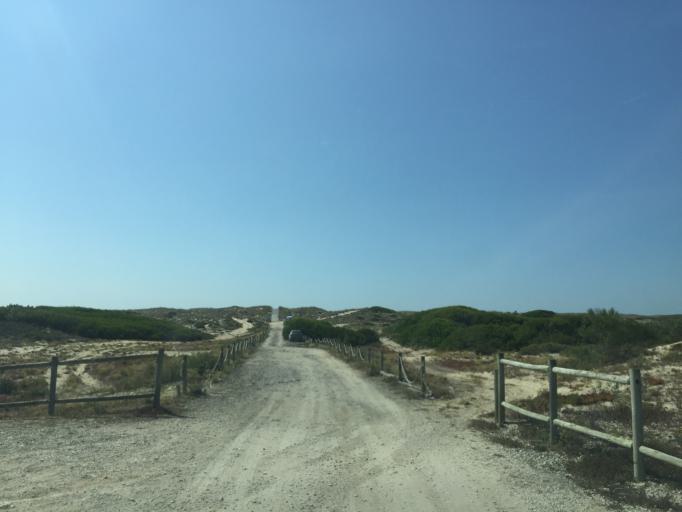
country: PT
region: Coimbra
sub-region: Figueira da Foz
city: Tavarede
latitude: 40.2645
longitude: -8.8678
